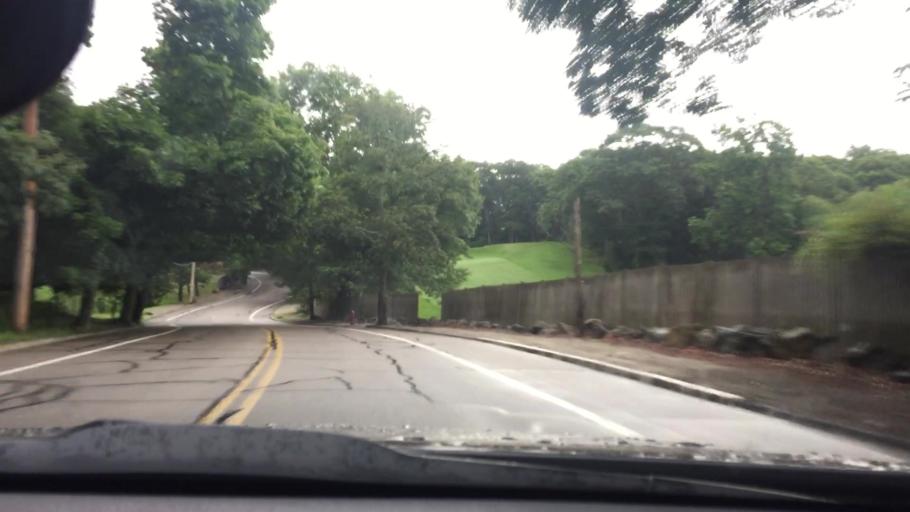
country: US
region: Massachusetts
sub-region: Middlesex County
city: Newton
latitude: 42.3000
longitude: -71.1929
